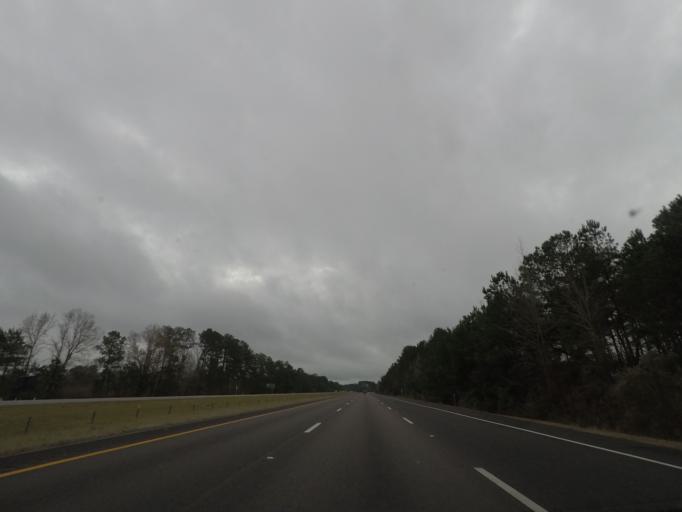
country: US
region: South Carolina
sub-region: Orangeburg County
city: Holly Hill
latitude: 33.4556
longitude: -80.4796
